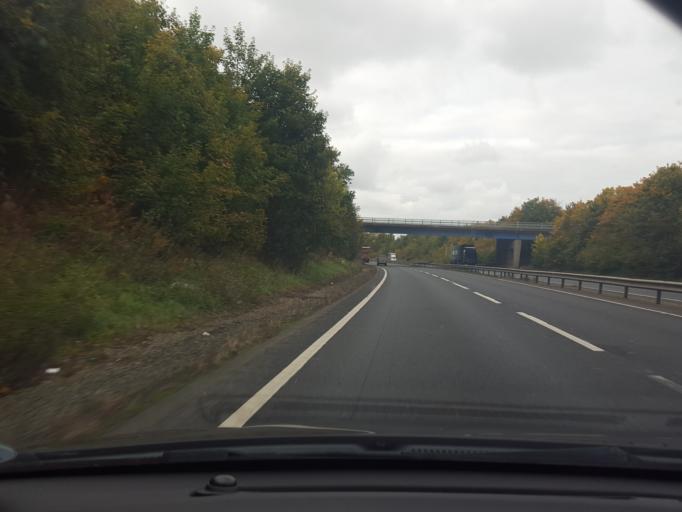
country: GB
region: England
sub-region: Suffolk
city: Stowmarket
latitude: 52.1941
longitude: 1.0120
